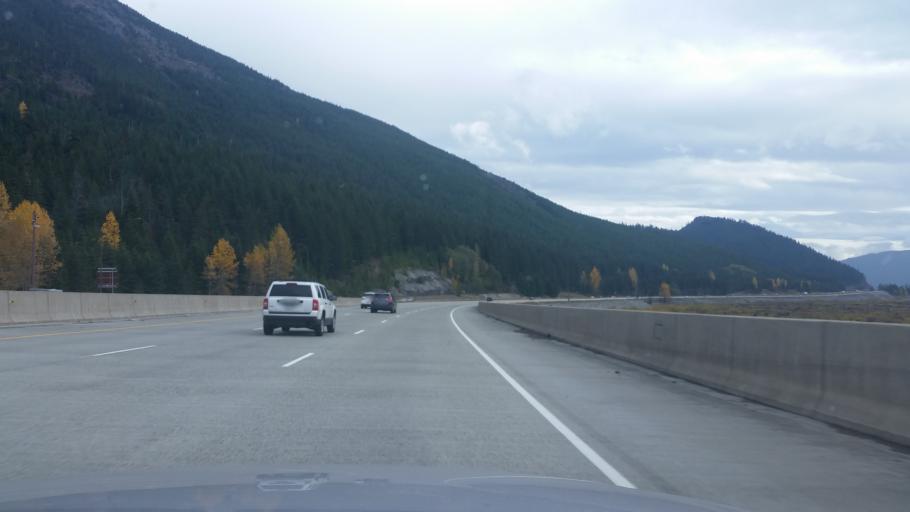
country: US
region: Washington
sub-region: King County
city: Tanner
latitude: 47.3903
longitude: -121.3834
